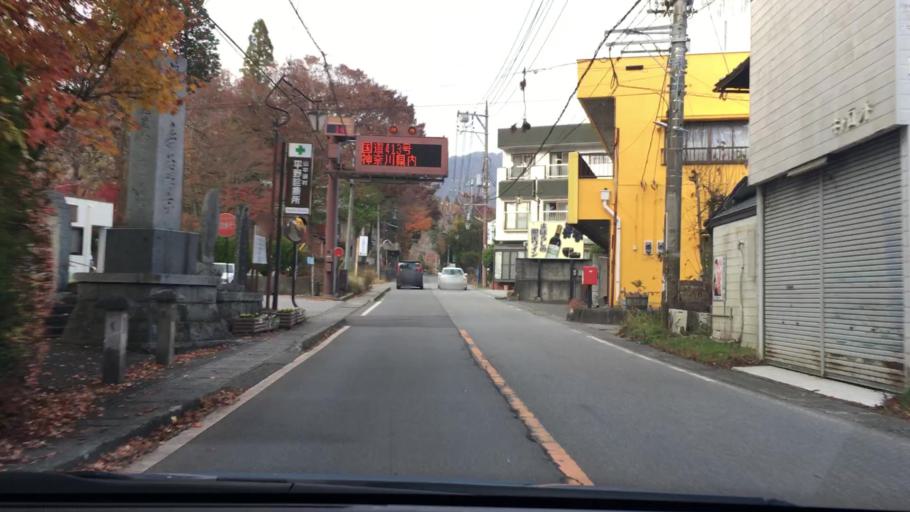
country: JP
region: Shizuoka
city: Gotemba
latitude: 35.4270
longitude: 138.9037
